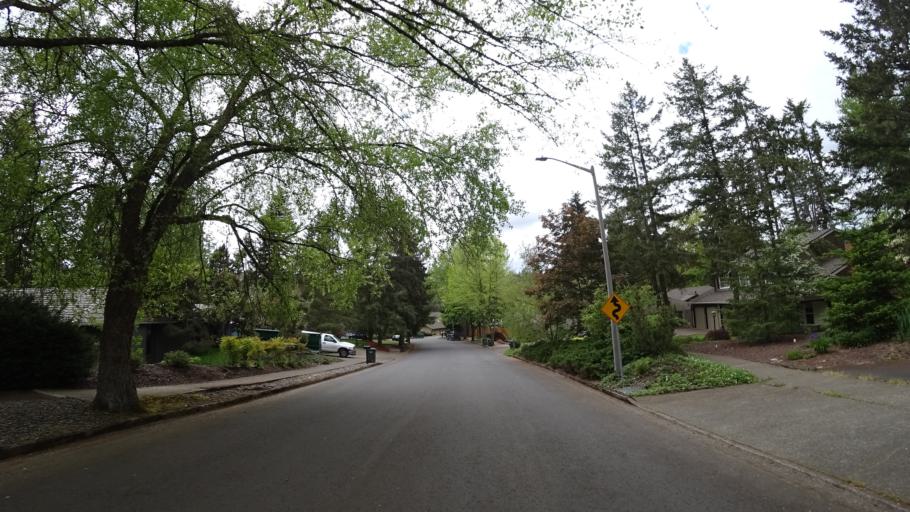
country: US
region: Oregon
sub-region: Washington County
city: Beaverton
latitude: 45.4775
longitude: -122.8290
